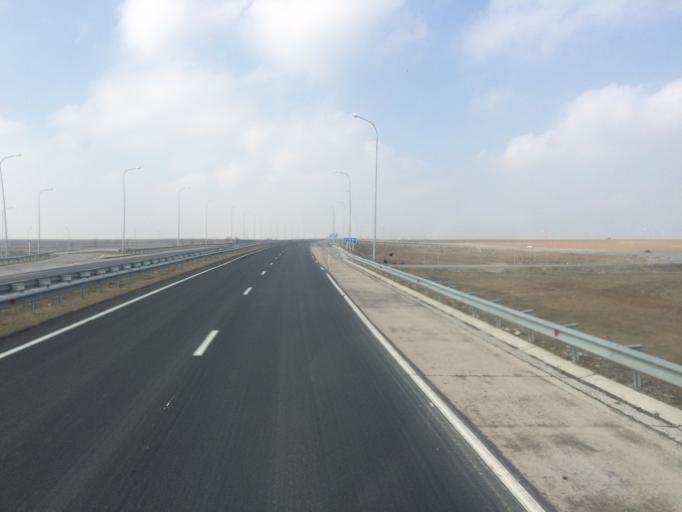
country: KZ
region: Ongtustik Qazaqstan
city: Temirlanovka
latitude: 42.5275
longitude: 69.3479
